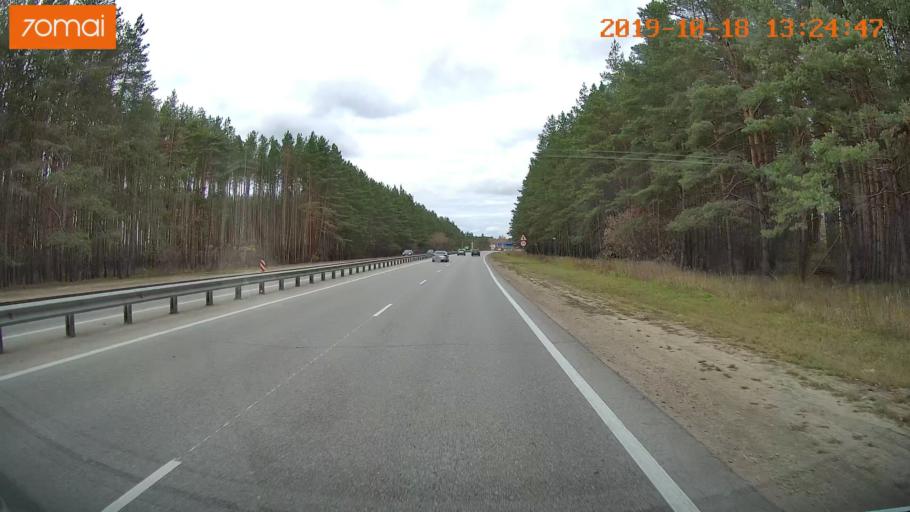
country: RU
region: Rjazan
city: Polyany
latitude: 54.7358
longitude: 39.8419
